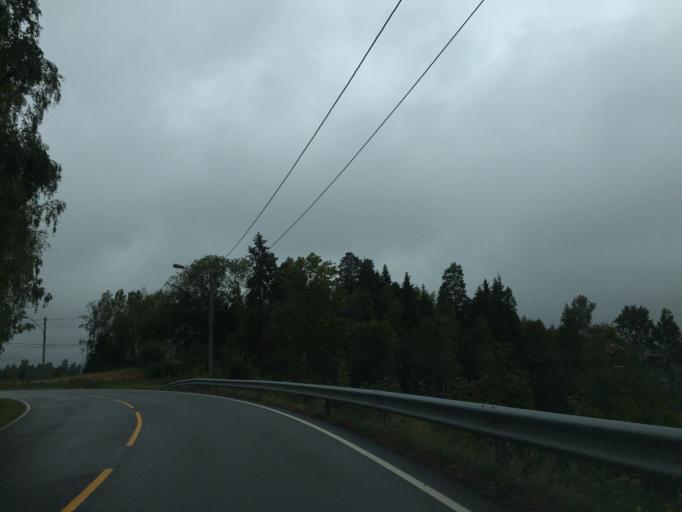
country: NO
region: Akershus
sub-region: Baerum
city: Lysaker
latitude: 60.0071
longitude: 10.6213
